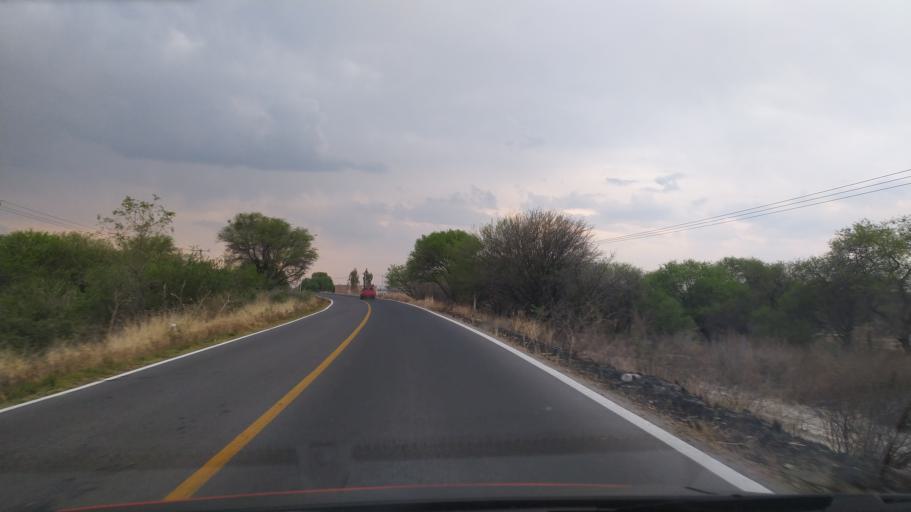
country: MX
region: Guanajuato
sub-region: San Francisco del Rincon
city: San Ignacio de Hidalgo
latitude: 20.8207
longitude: -101.9024
